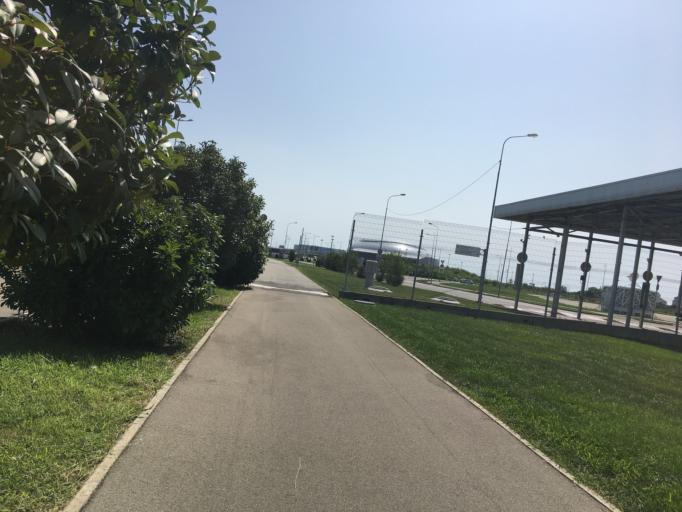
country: RU
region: Krasnodarskiy
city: Adler
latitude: 43.4130
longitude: 39.9488
